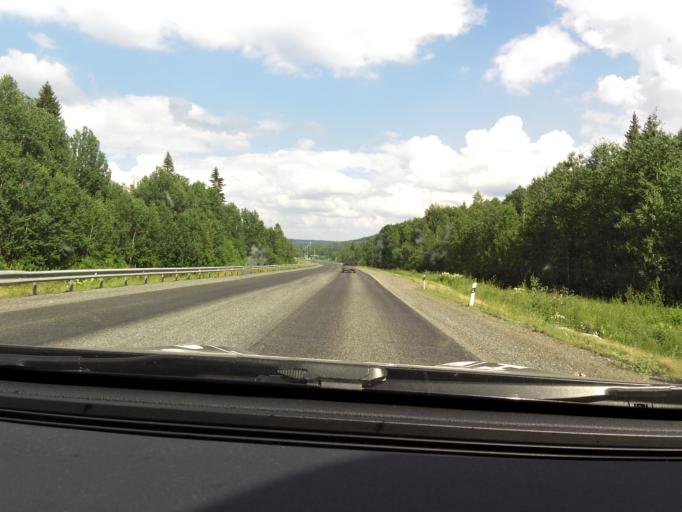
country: RU
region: Sverdlovsk
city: Arti
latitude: 56.7902
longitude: 58.5959
